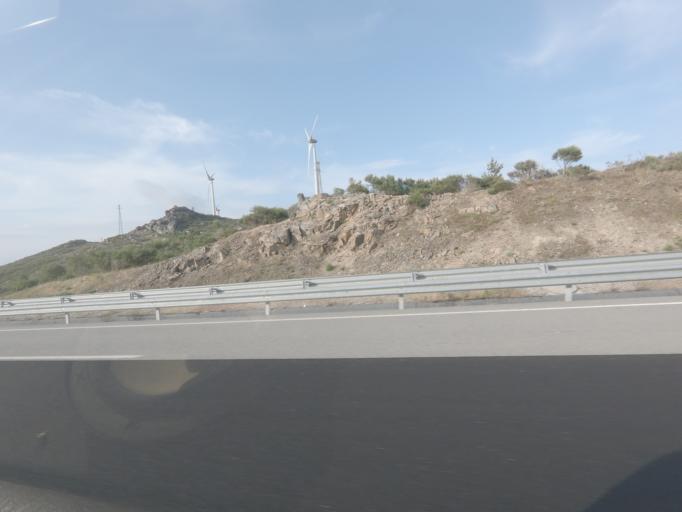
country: PT
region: Vila Real
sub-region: Vila Pouca de Aguiar
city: Vila Pouca de Aguiar
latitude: 41.4436
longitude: -7.6464
